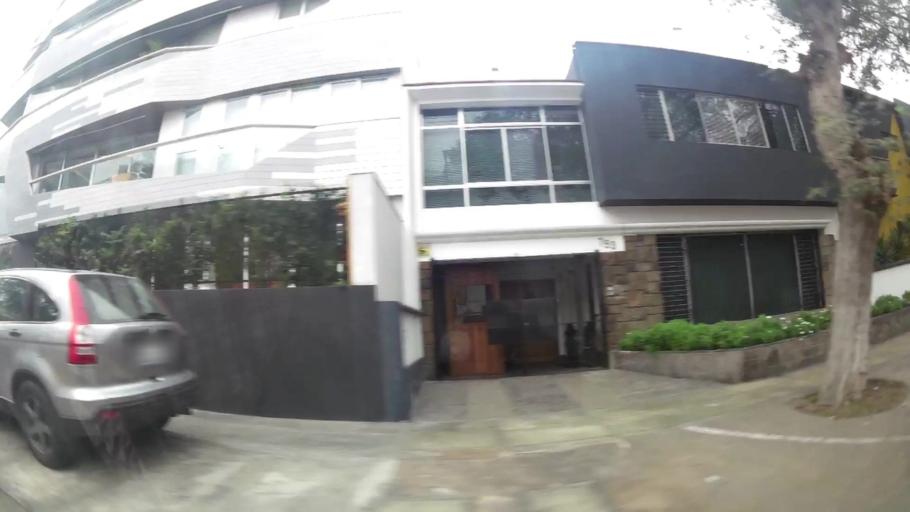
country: PE
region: Lima
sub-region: Lima
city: Surco
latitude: -12.1308
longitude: -77.0273
